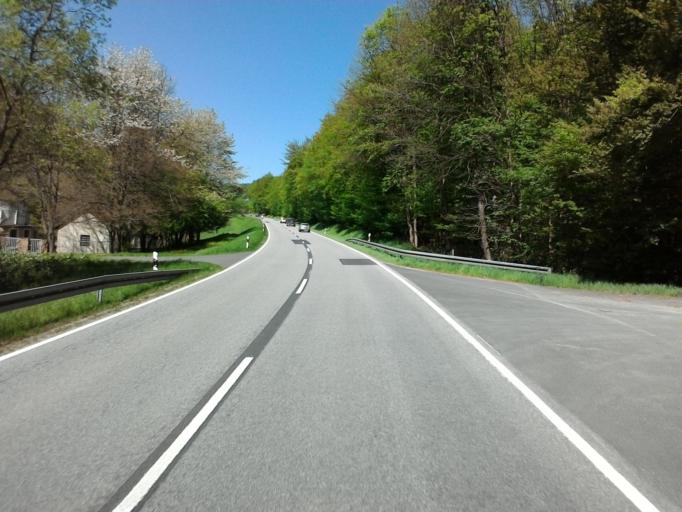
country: DE
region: Bavaria
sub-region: Regierungsbezirk Unterfranken
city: Rechtenbach
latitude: 49.9768
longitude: 9.5203
